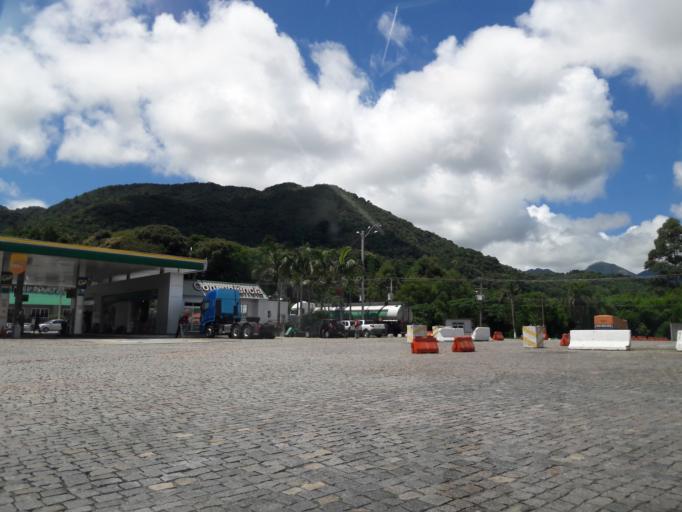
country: BR
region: Parana
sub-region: Campina Grande Do Sul
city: Campina Grande do Sul
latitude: -25.1768
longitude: -48.8740
